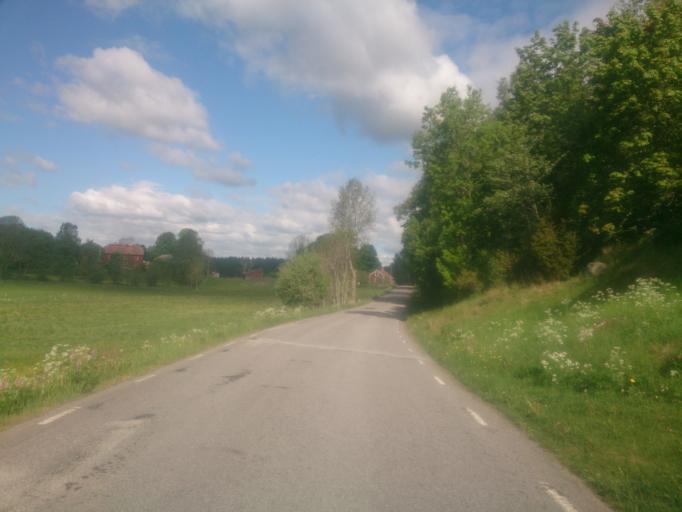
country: SE
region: OEstergoetland
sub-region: Atvidabergs Kommun
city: Atvidaberg
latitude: 58.3336
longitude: 16.0336
